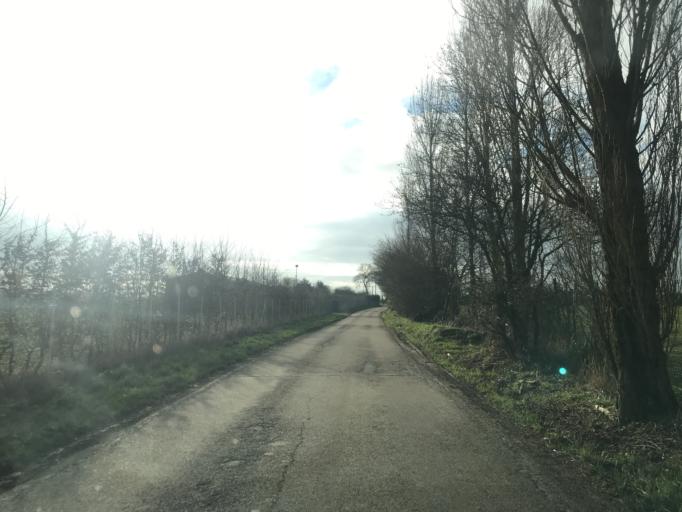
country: FR
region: Lower Normandy
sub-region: Departement du Calvados
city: Dozule
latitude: 49.2206
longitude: -0.1030
